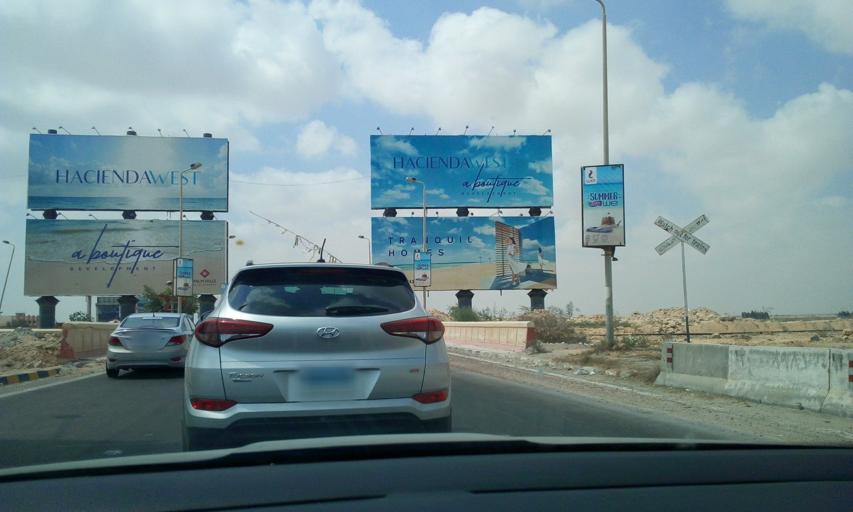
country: EG
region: Muhafazat Matruh
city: Al `Alamayn
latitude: 30.8165
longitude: 28.9840
